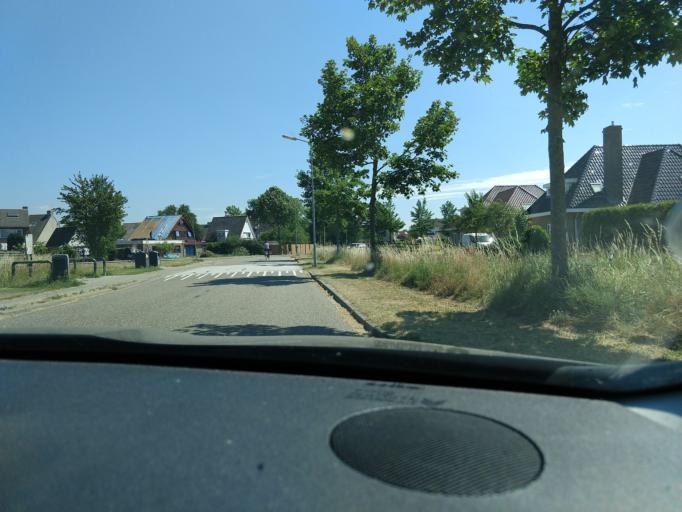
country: NL
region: Zeeland
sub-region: Gemeente Veere
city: Veere
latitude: 51.5061
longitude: 3.6707
